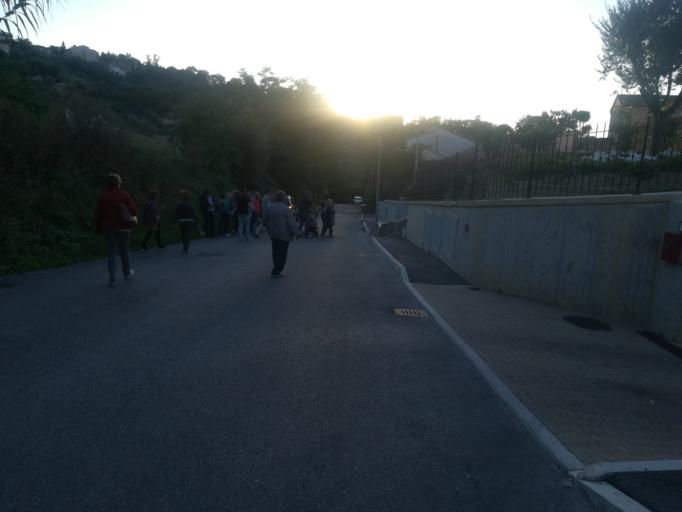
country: IT
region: The Marches
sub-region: Provincia di Macerata
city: Villa Potenza
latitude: 43.3031
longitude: 13.4336
